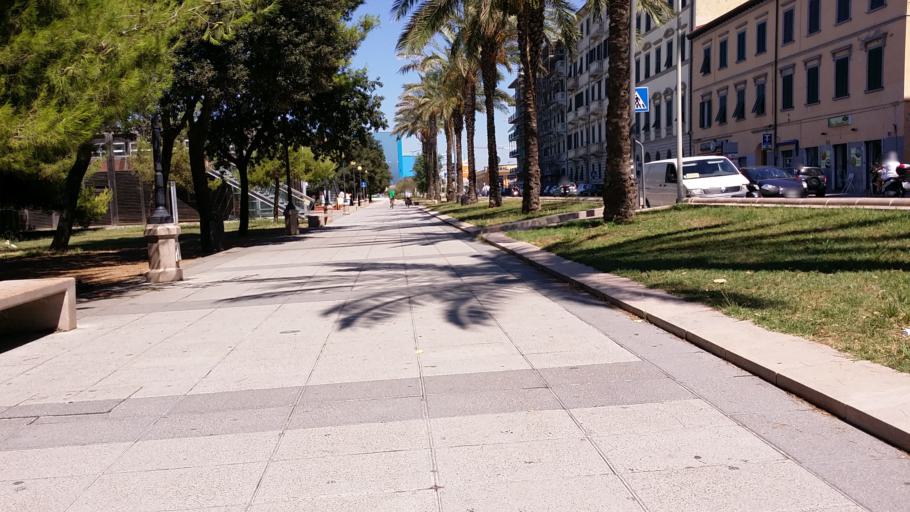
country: IT
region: Tuscany
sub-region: Provincia di Livorno
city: Livorno
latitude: 43.5387
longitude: 10.3019
